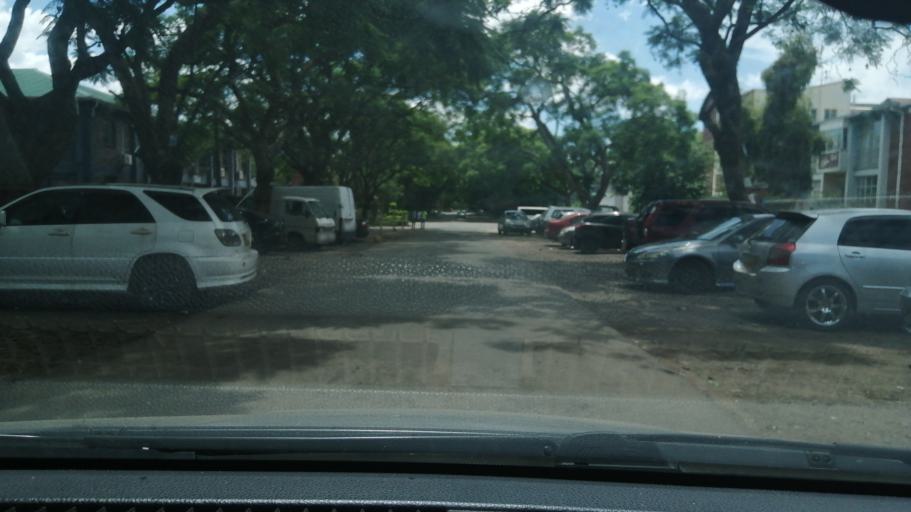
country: ZW
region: Harare
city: Harare
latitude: -17.8202
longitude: 31.0601
